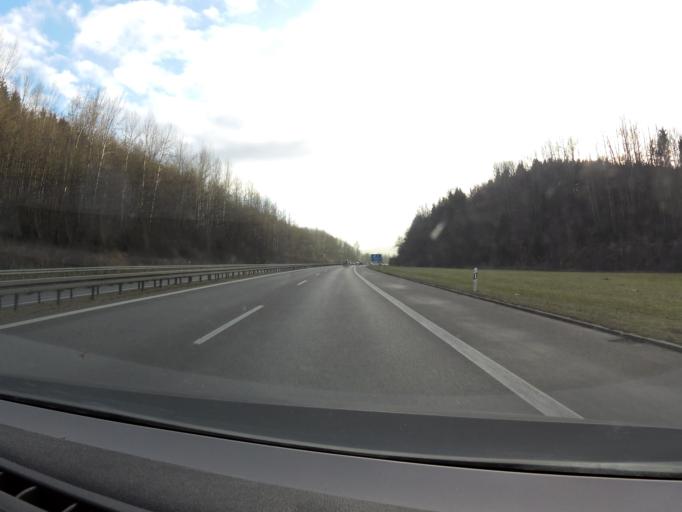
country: DE
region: Bavaria
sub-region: Upper Bavaria
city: Sindelsdorf
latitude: 47.7392
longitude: 11.3312
